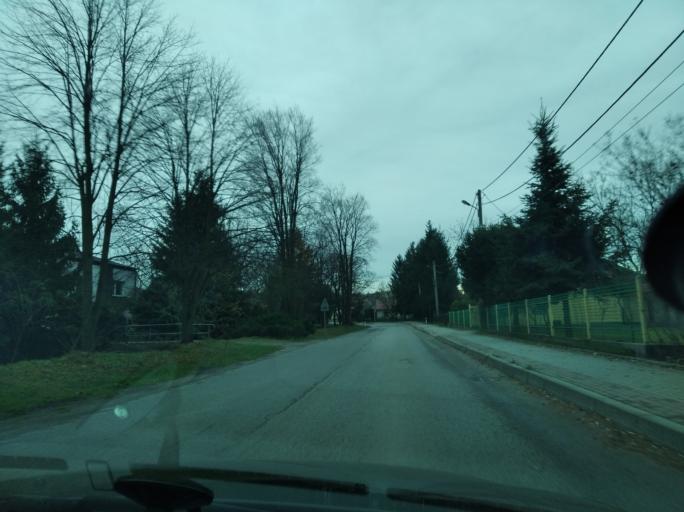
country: PL
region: Subcarpathian Voivodeship
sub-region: Powiat lancucki
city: Krzemienica
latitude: 50.0805
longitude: 22.1896
